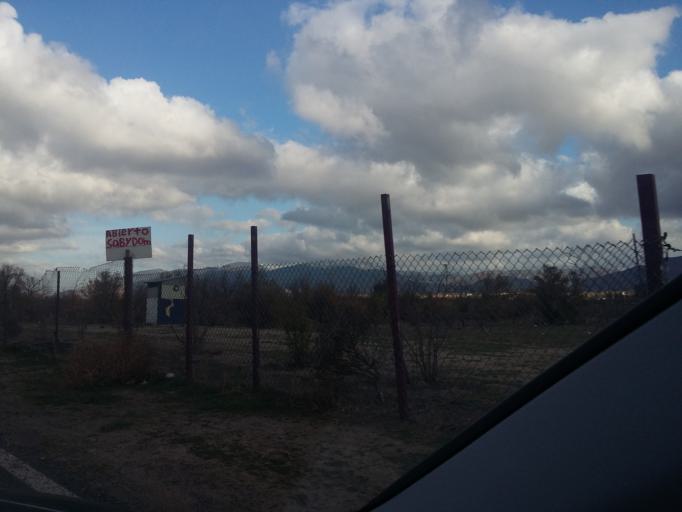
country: MX
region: Baja California
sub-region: Ensenada
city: Rancho Verde
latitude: 32.0534
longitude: -116.6512
